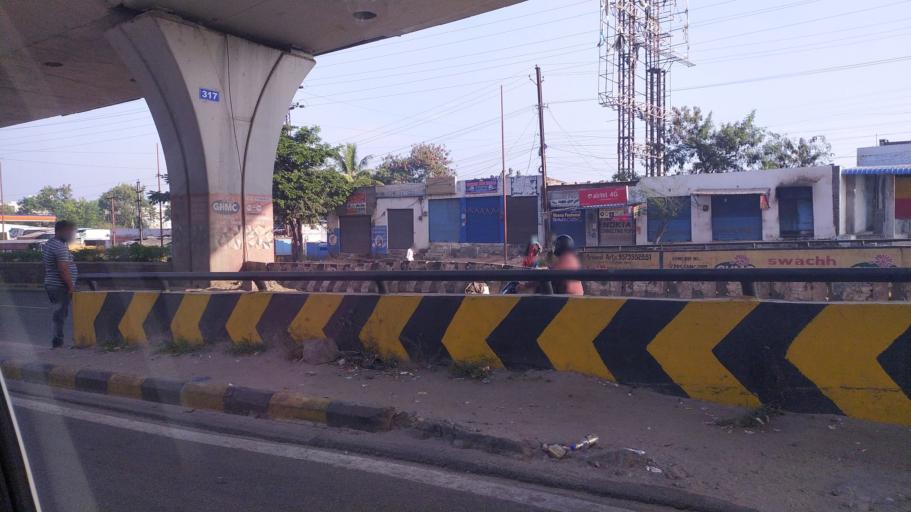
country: IN
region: Telangana
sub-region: Hyderabad
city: Hyderabad
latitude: 17.3223
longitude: 78.4310
